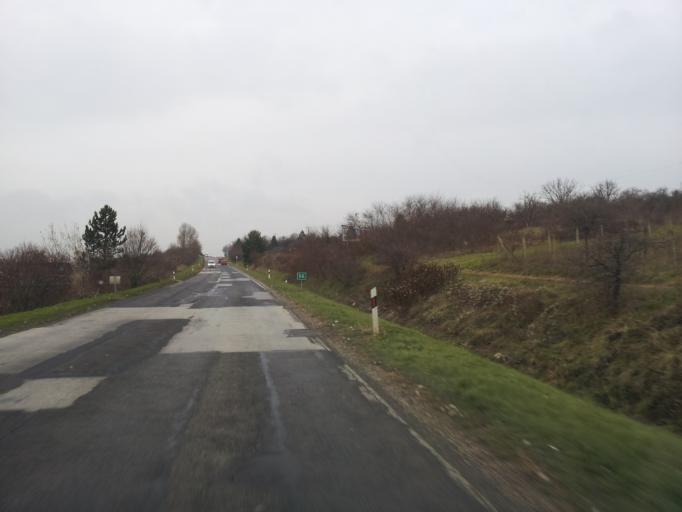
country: HU
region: Veszprem
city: Veszprem
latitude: 47.0979
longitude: 17.8736
